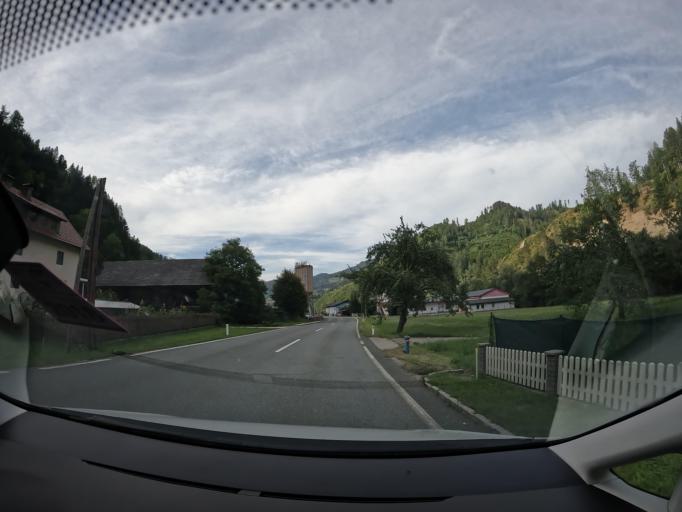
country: AT
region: Carinthia
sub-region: Politischer Bezirk Volkermarkt
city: Bad Eisenkappel
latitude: 46.4699
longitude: 14.5926
